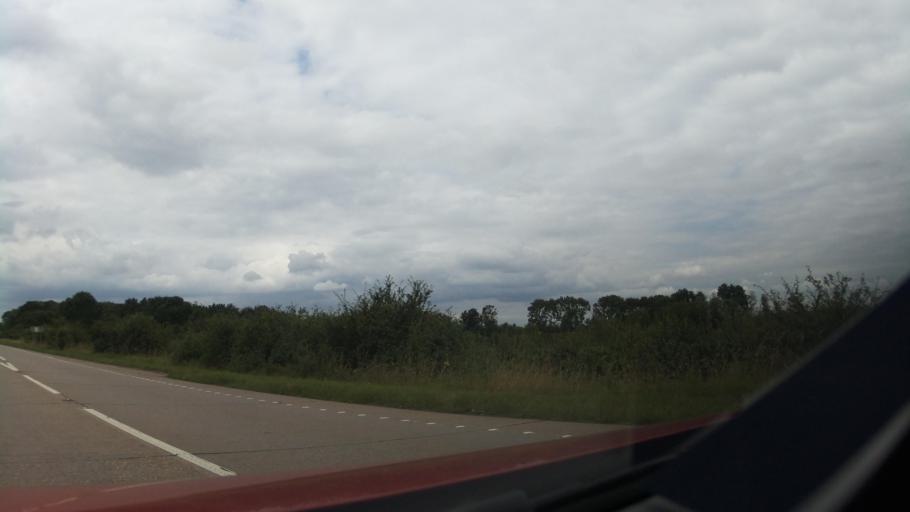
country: GB
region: England
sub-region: Lincolnshire
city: Long Bennington
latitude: 52.9380
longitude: -0.8327
